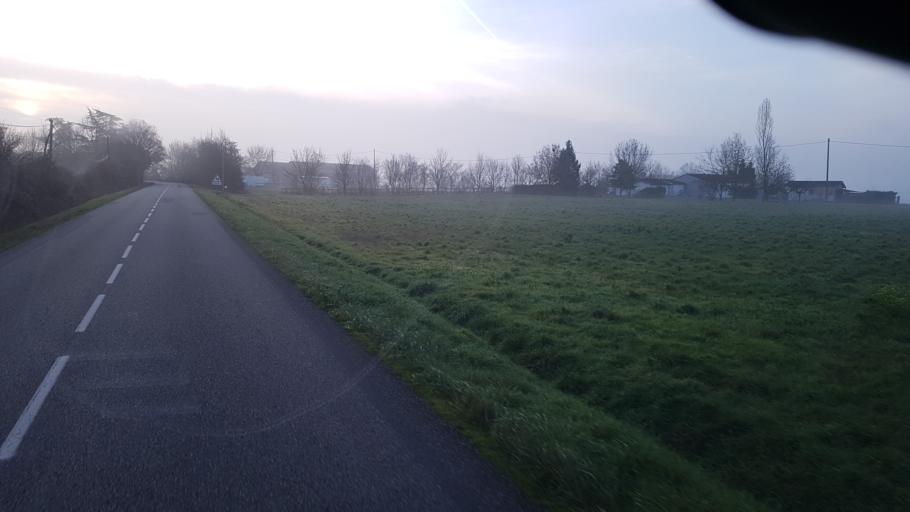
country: FR
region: Midi-Pyrenees
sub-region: Departement du Tarn-et-Garonne
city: Monteils
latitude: 44.1412
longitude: 1.5637
